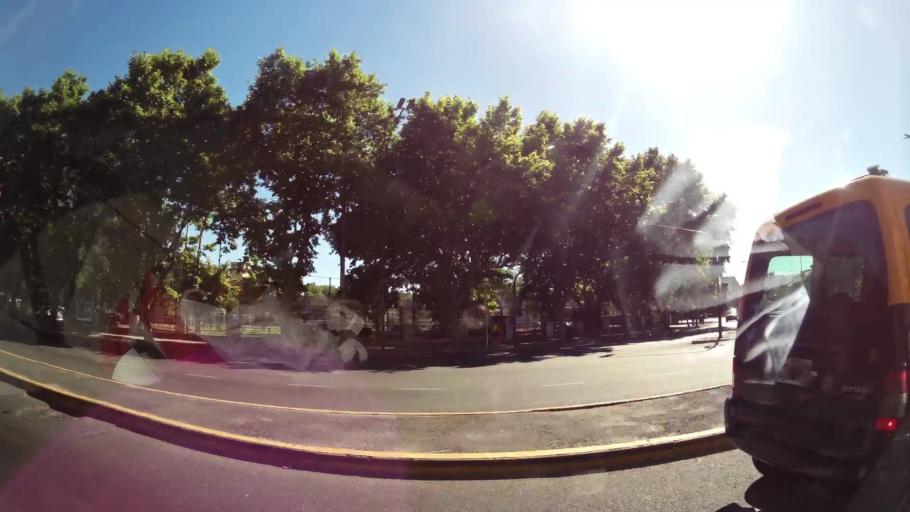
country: AR
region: Buenos Aires F.D.
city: Colegiales
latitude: -34.5488
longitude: -58.4550
